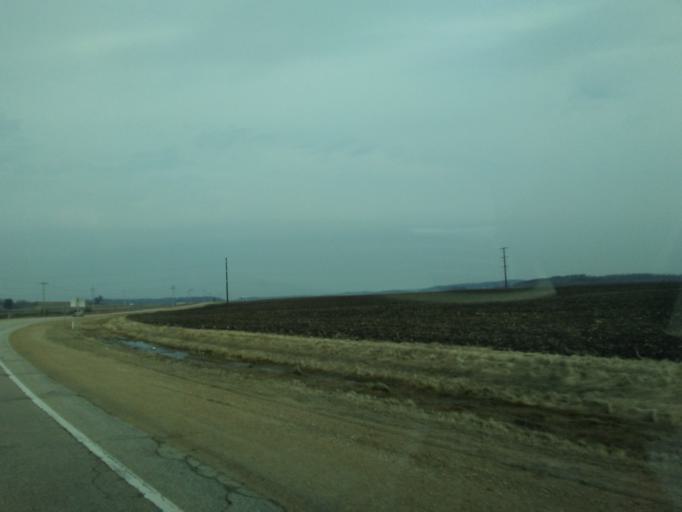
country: US
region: Wisconsin
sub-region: Columbia County
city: Lodi
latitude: 43.2528
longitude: -89.5206
